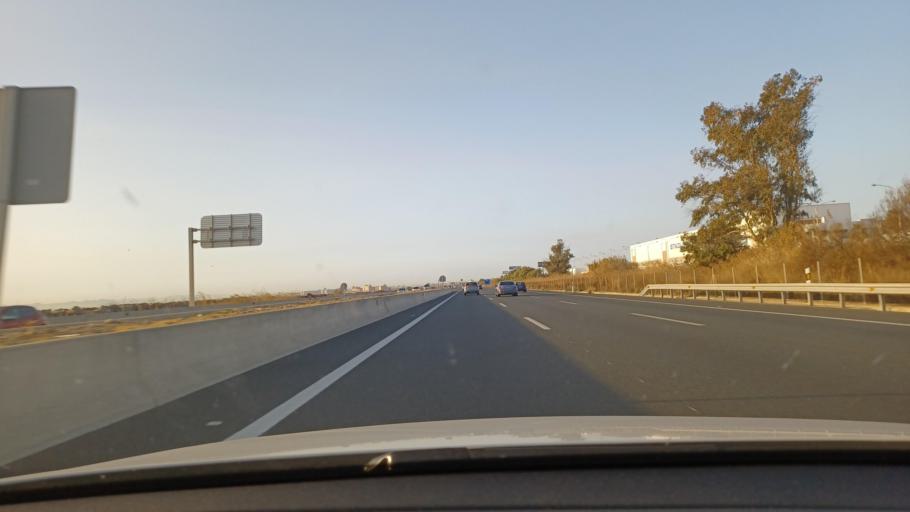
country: ES
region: Valencia
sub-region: Provincia de Valencia
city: Albuixech
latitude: 39.5412
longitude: -0.3042
